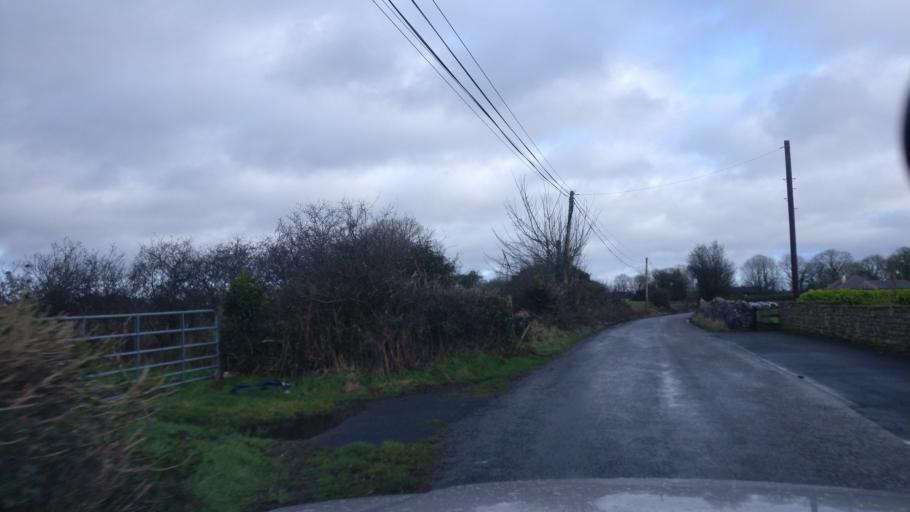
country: IE
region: Connaught
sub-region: County Galway
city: Loughrea
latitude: 53.2585
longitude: -8.6305
